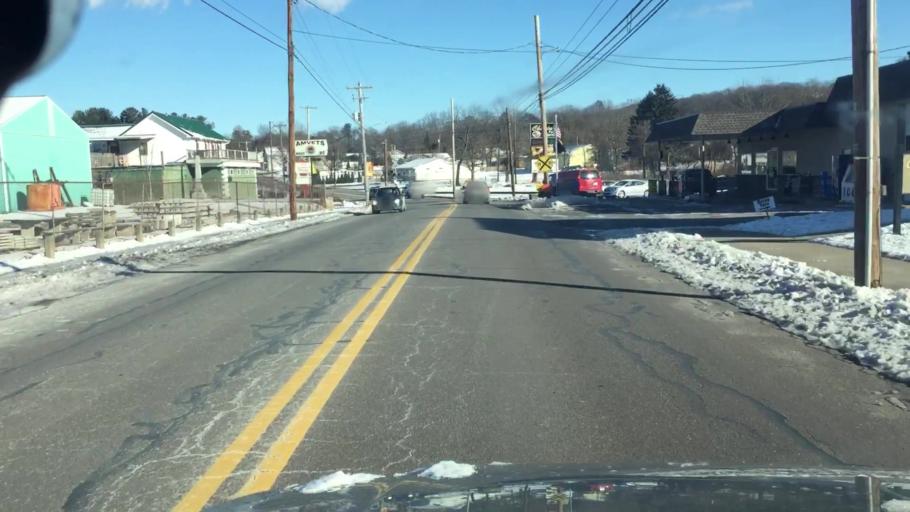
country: US
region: Pennsylvania
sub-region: Luzerne County
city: Nescopeck
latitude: 41.0524
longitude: -76.2123
